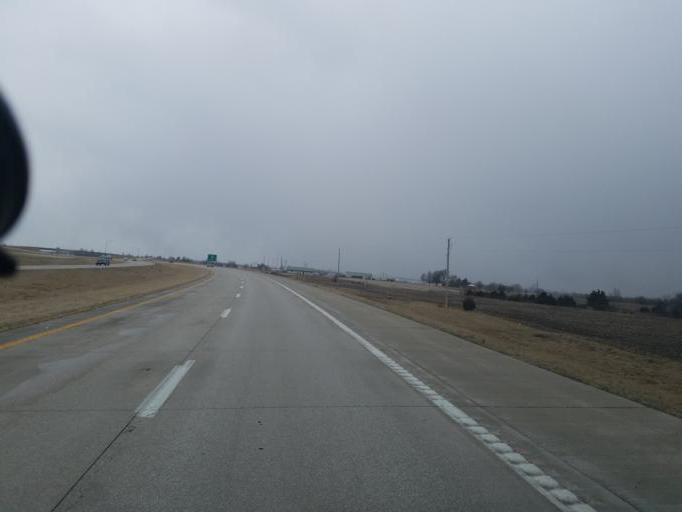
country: US
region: Missouri
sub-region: Randolph County
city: Moberly
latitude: 39.4616
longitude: -92.4352
